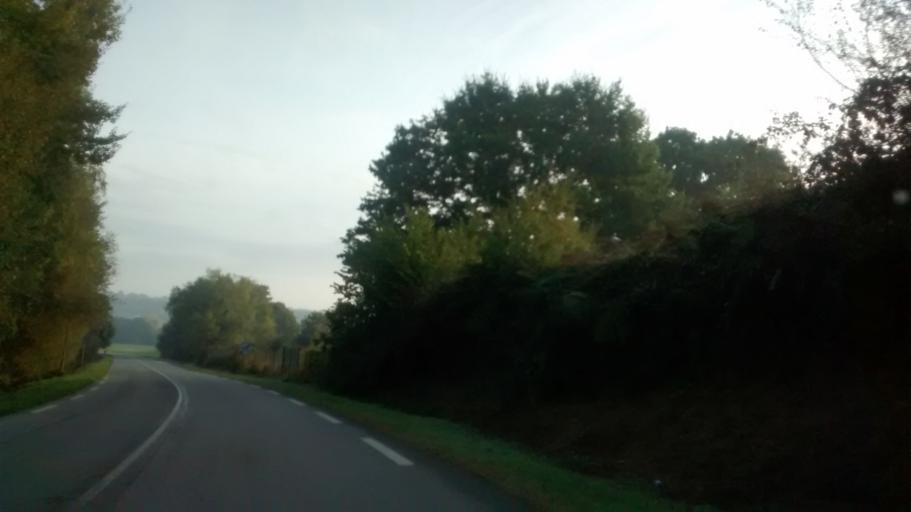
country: FR
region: Brittany
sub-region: Departement d'Ille-et-Vilaine
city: Poce-les-Bois
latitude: 48.0890
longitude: -1.2376
